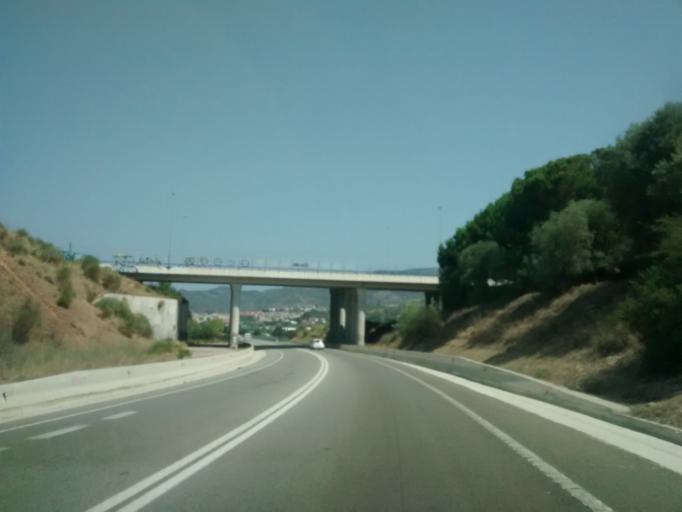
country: ES
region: Catalonia
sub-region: Provincia de Barcelona
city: Abrera
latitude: 41.5269
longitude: 1.9061
